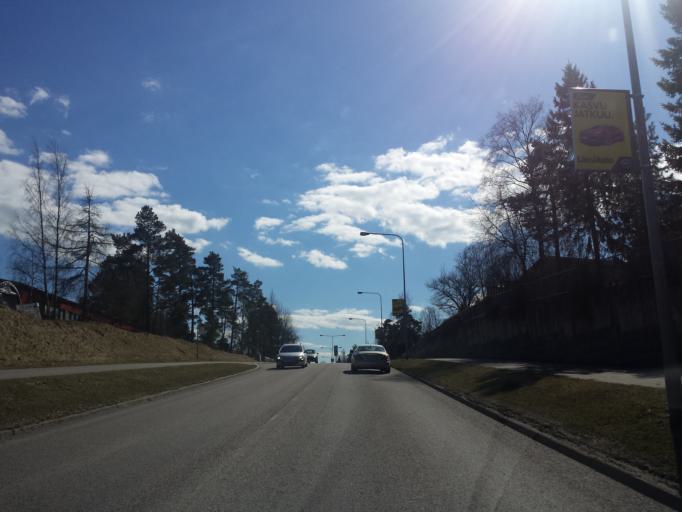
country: FI
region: Uusimaa
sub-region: Helsinki
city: Vantaa
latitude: 60.2681
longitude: 25.0718
